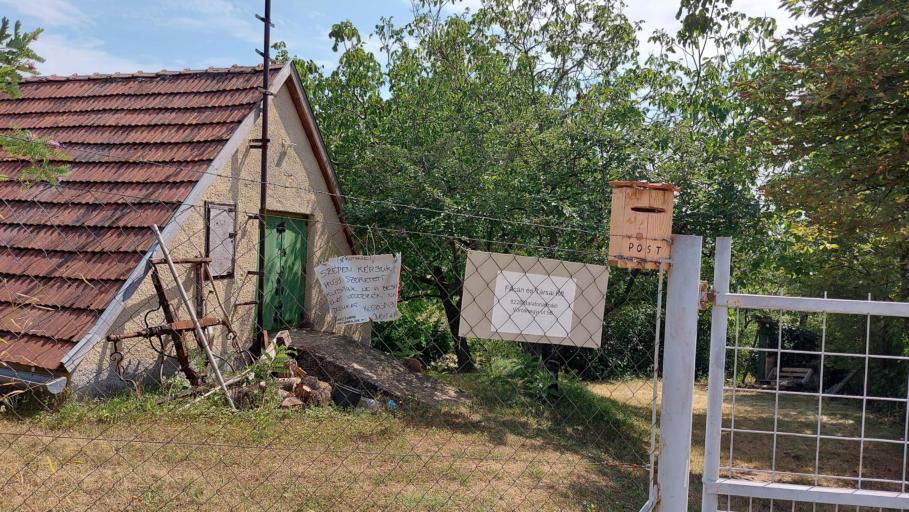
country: HU
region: Veszprem
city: Szentkiralyszabadja
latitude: 47.0453
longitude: 17.9947
